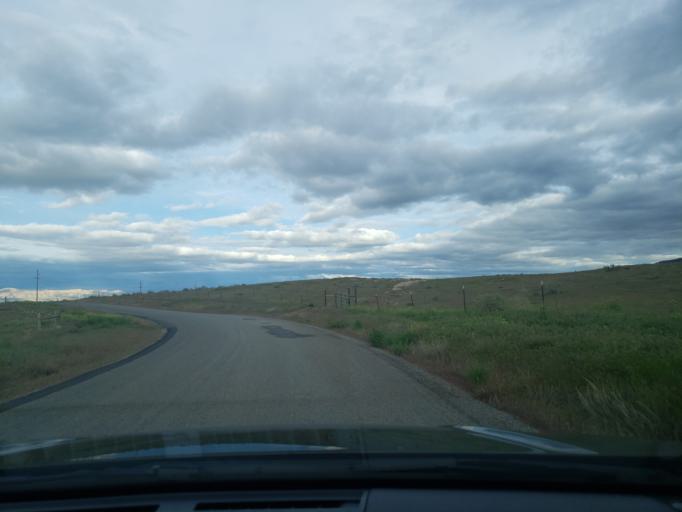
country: US
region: Colorado
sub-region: Mesa County
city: Fruita
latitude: 39.1400
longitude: -108.7520
